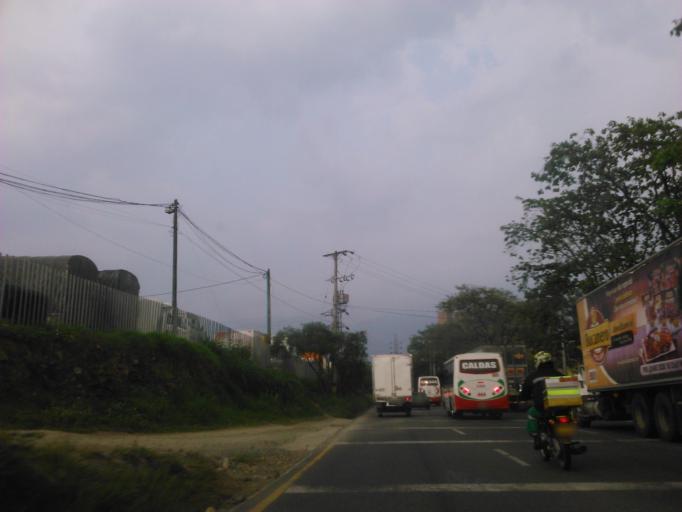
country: CO
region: Antioquia
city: Sabaneta
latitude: 6.1516
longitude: -75.6292
